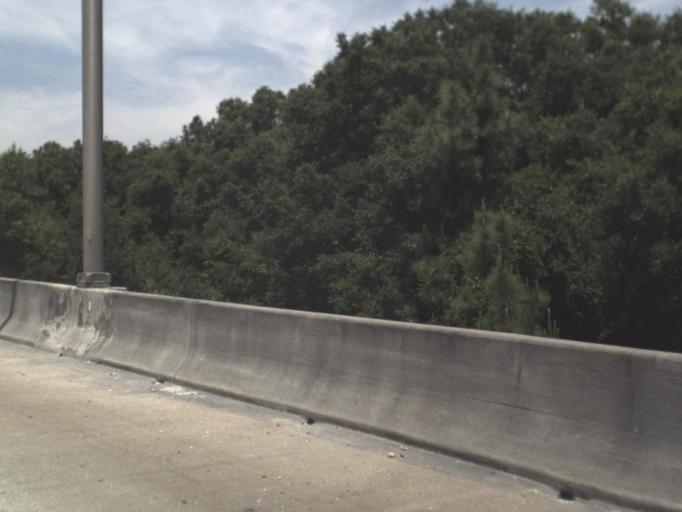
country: US
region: Florida
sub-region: Duval County
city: Jacksonville
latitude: 30.4386
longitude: -81.5865
